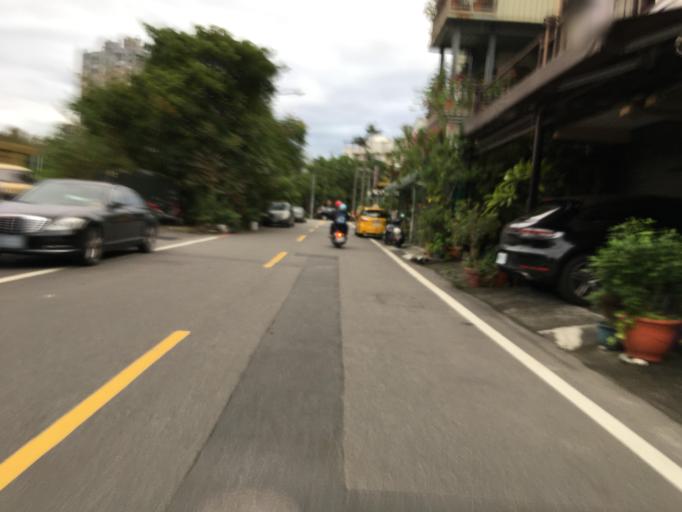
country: TW
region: Taiwan
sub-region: Yilan
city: Yilan
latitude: 24.6842
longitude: 121.7686
